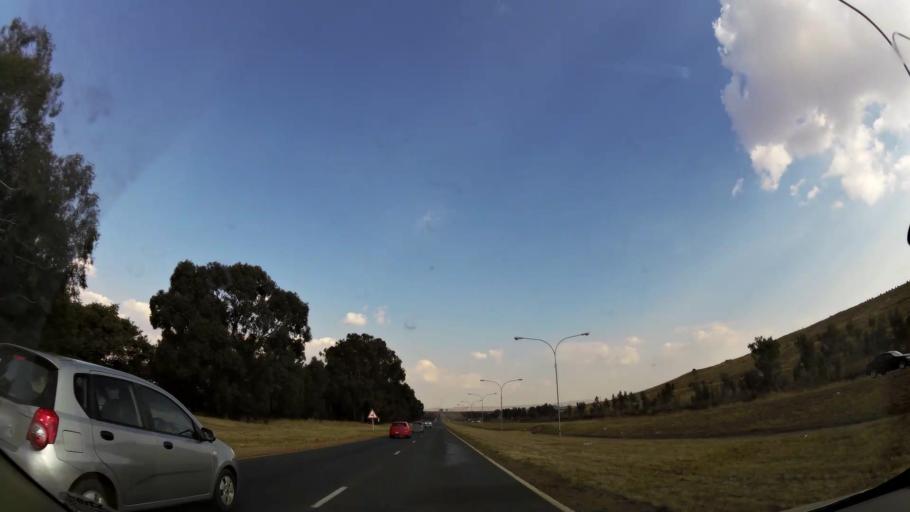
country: ZA
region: Gauteng
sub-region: Ekurhuleni Metropolitan Municipality
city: Springs
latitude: -26.3522
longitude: 28.3416
